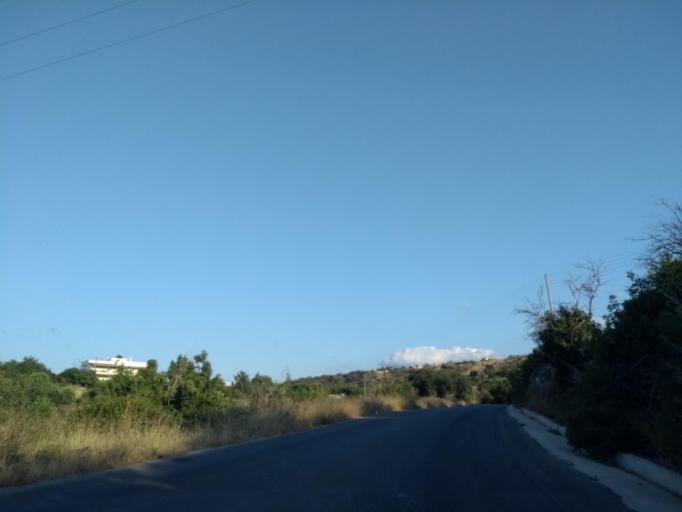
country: GR
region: Crete
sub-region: Nomos Chanias
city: Kalivai
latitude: 35.4280
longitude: 24.1807
